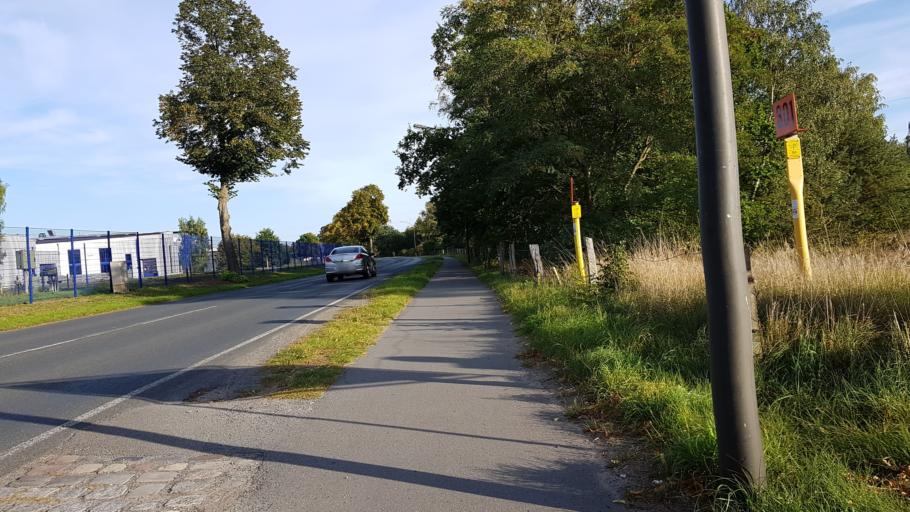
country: DE
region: Lower Saxony
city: Oyten
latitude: 53.0242
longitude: 8.9852
